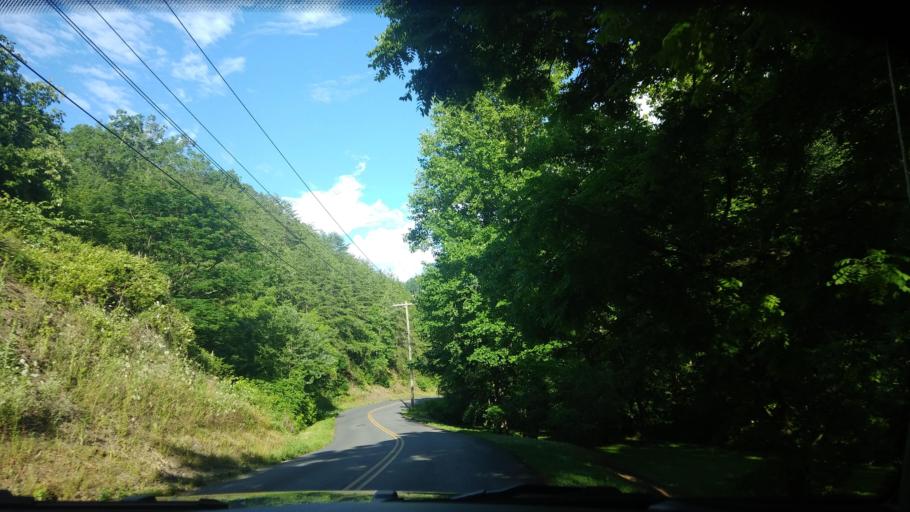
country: US
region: Tennessee
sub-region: Sevier County
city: Pigeon Forge
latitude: 35.7670
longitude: -83.5971
